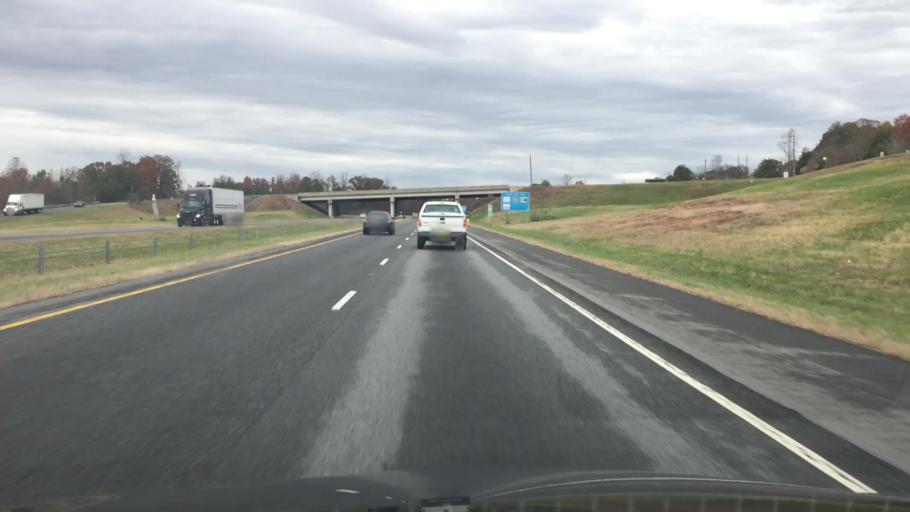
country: US
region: North Carolina
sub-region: Rockingham County
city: Reidsville
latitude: 36.3094
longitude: -79.6442
